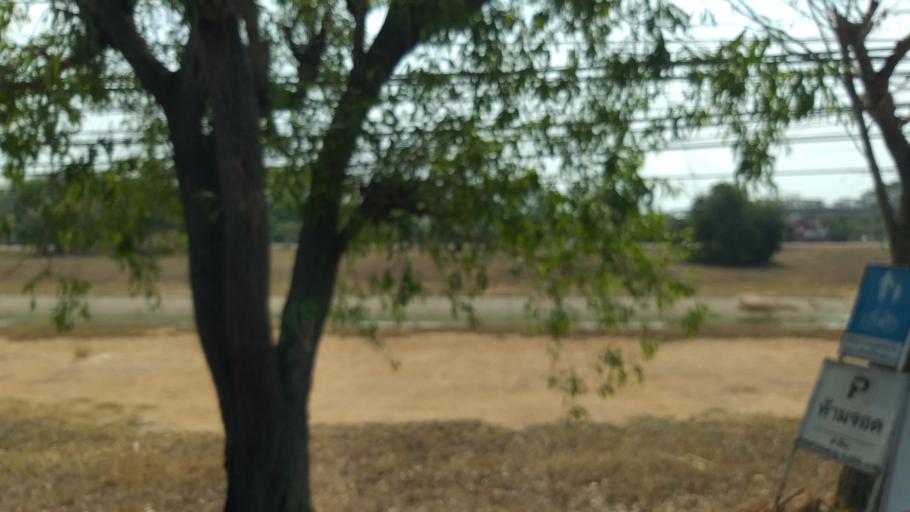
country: TH
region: Changwat Udon Thani
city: Udon Thani
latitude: 17.3855
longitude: 102.7758
